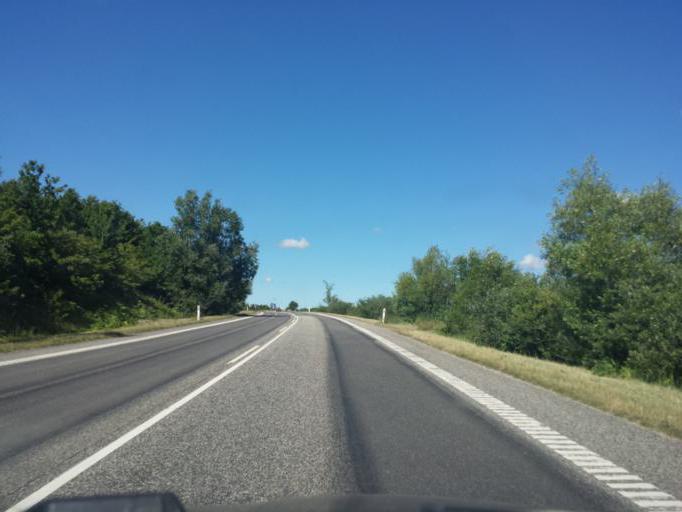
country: DK
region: Capital Region
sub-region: Egedal Kommune
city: Smorumnedre
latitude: 55.7586
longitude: 12.2920
